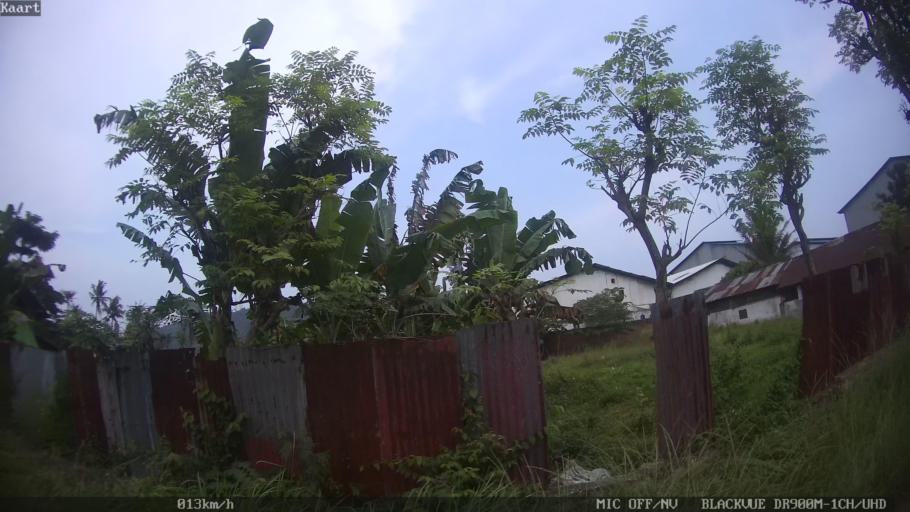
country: ID
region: Lampung
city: Panjang
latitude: -5.4311
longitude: 105.3279
